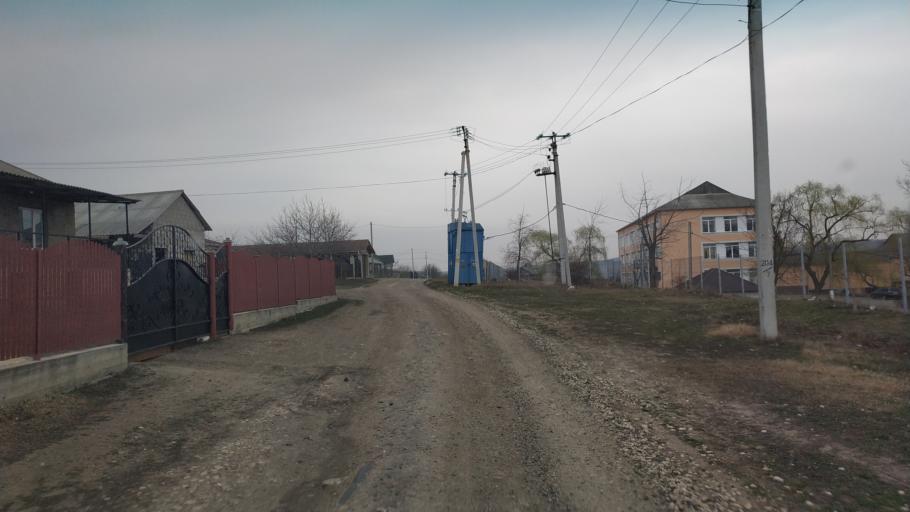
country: MD
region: Chisinau
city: Singera
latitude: 46.8311
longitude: 28.9689
